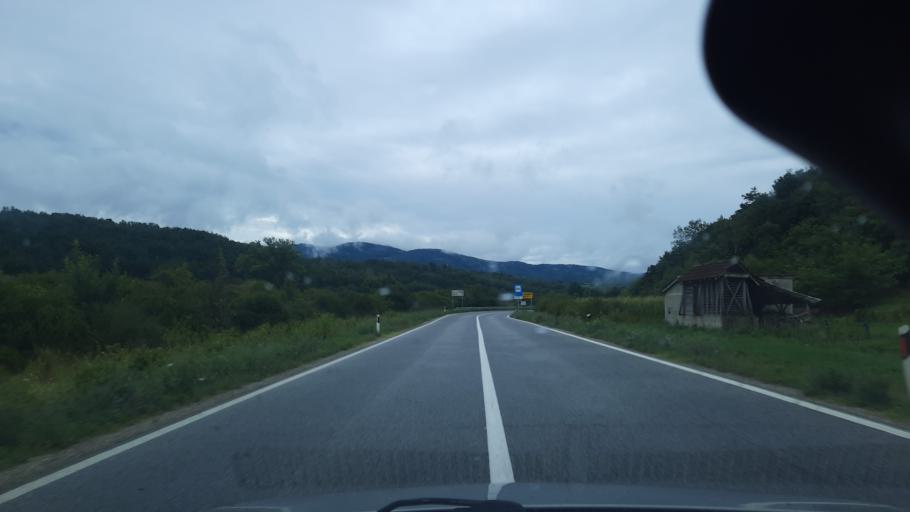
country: RS
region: Central Serbia
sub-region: Sumadijski Okrug
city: Knic
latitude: 43.8326
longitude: 20.7792
